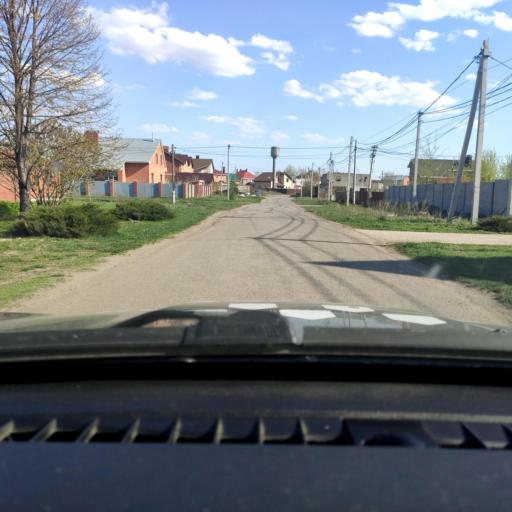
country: RU
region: Samara
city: Tol'yatti
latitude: 53.5665
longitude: 49.3799
